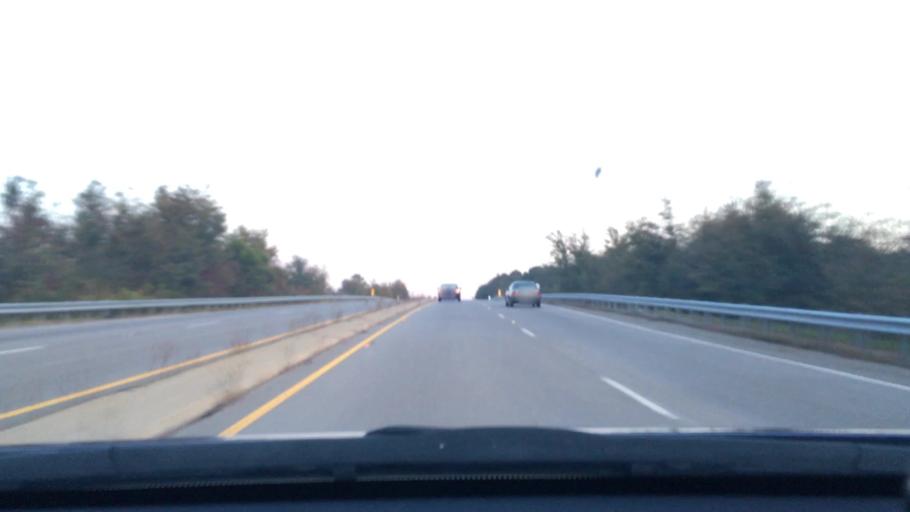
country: US
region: South Carolina
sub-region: Richland County
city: Gadsden
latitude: 33.9427
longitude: -80.6891
